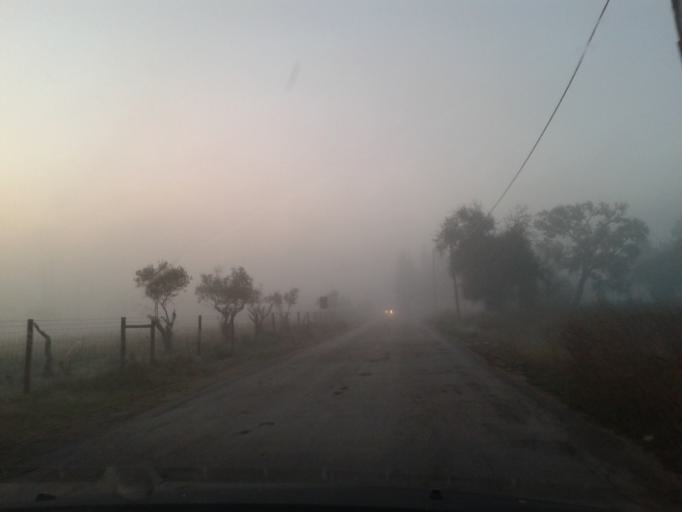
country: PT
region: Setubal
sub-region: Palmela
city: Palmela
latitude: 38.5996
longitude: -8.8968
